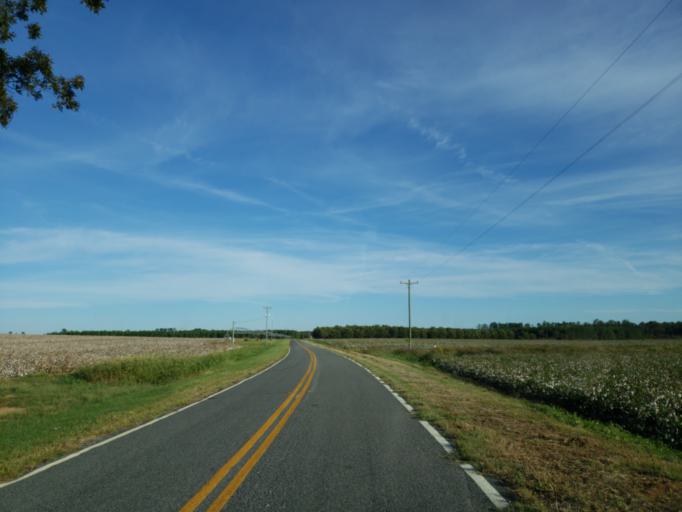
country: US
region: Georgia
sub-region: Dooly County
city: Vienna
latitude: 32.0658
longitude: -83.7757
